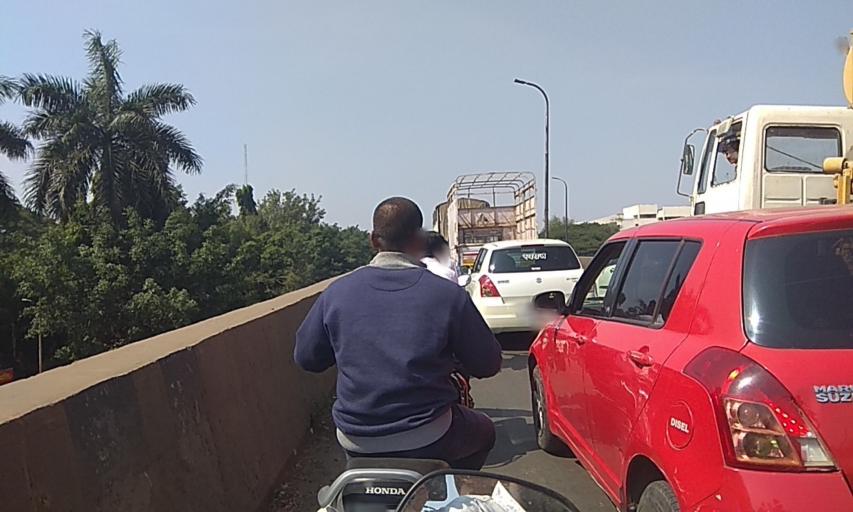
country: IN
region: Maharashtra
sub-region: Pune Division
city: Pune
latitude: 18.5022
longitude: 73.9282
